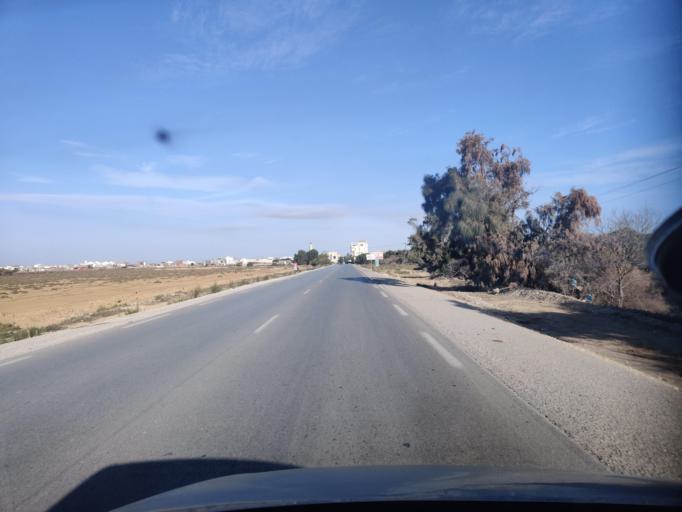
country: TN
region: Ariana
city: Ariana
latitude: 36.9516
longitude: 10.2354
